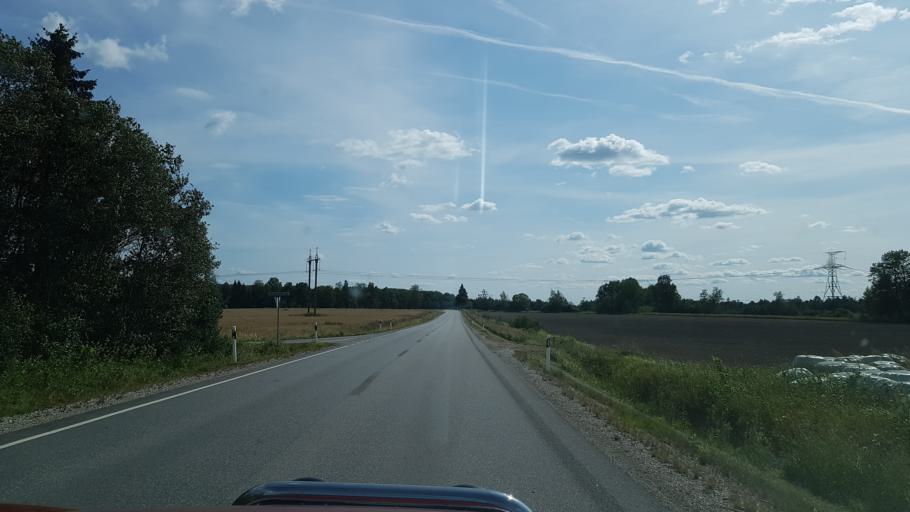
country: EE
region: Jogevamaa
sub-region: Mustvee linn
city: Mustvee
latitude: 58.8943
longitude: 26.8131
